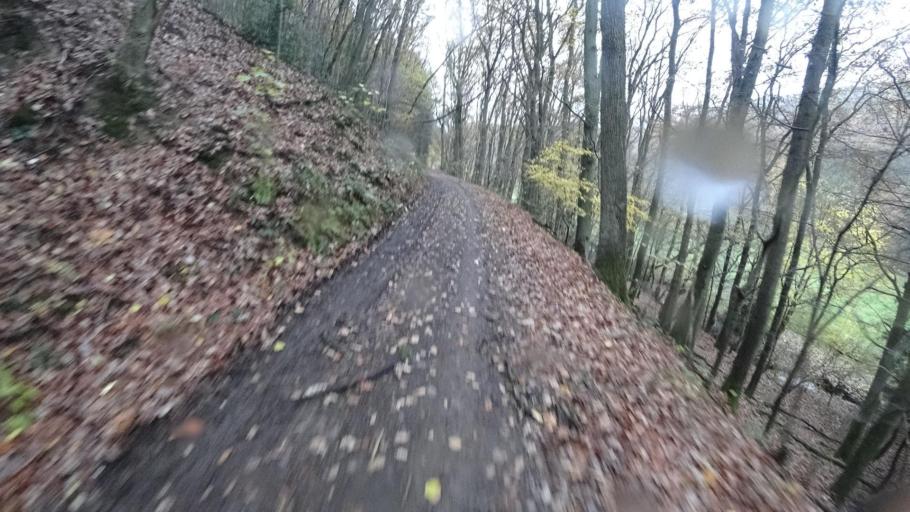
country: DE
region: Rheinland-Pfalz
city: Bad Neuenahr-Ahrweiler
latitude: 50.5270
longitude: 7.0930
